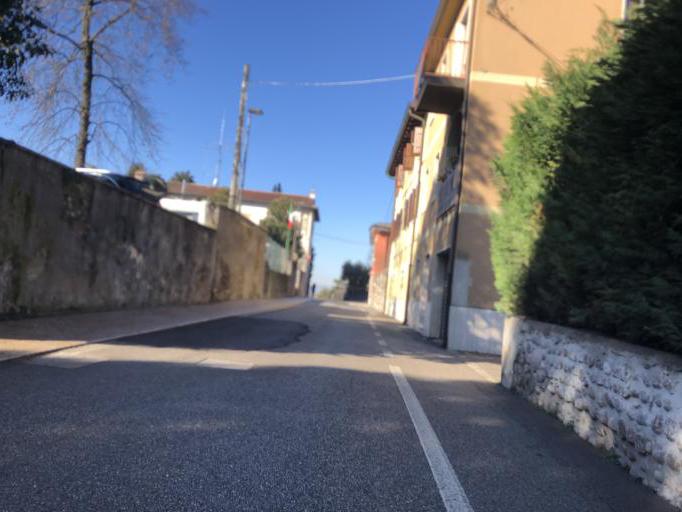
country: IT
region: Veneto
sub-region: Provincia di Verona
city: Sona
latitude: 45.4347
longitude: 10.8319
